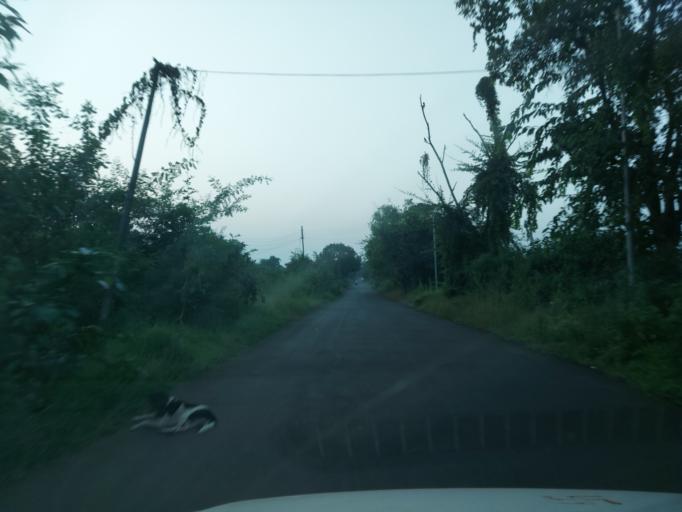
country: IN
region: Maharashtra
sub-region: Sindhudurg
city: Kudal
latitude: 16.1038
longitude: 73.7080
